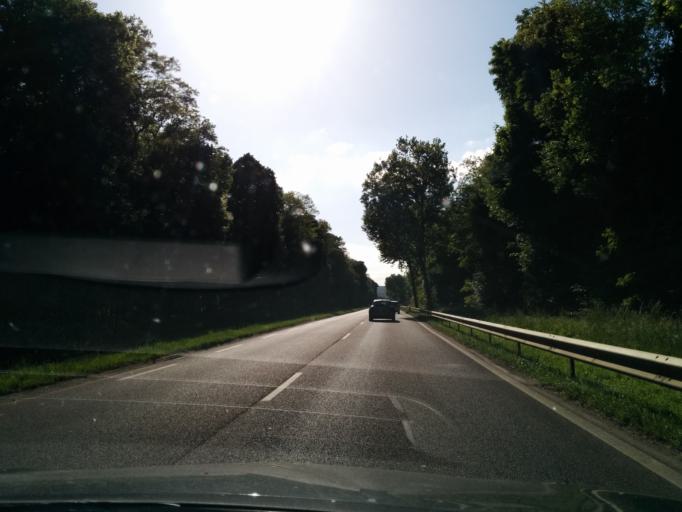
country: FR
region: Ile-de-France
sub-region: Departement des Yvelines
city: Buchelay
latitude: 48.9984
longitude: 1.6576
